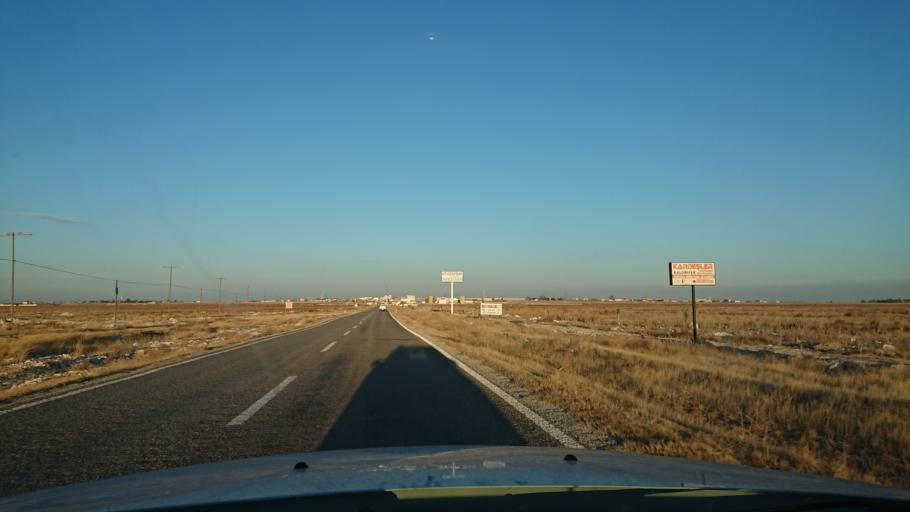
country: TR
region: Aksaray
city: Eskil
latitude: 38.3868
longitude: 33.3817
